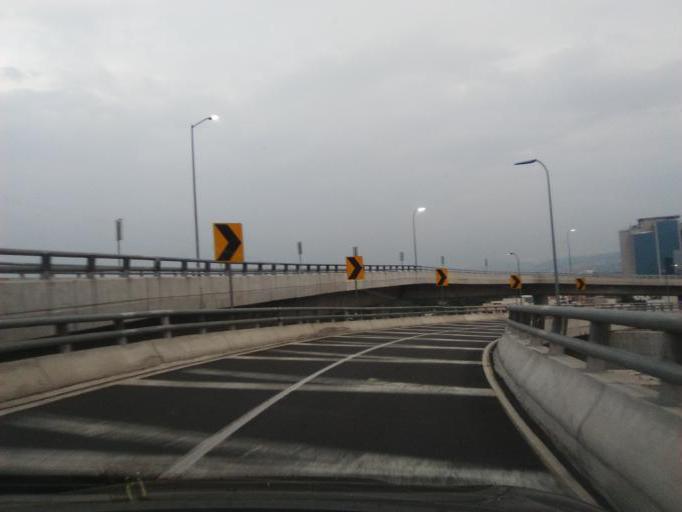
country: MX
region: Mexico City
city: Magdalena Contreras
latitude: 19.3214
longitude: -99.2210
